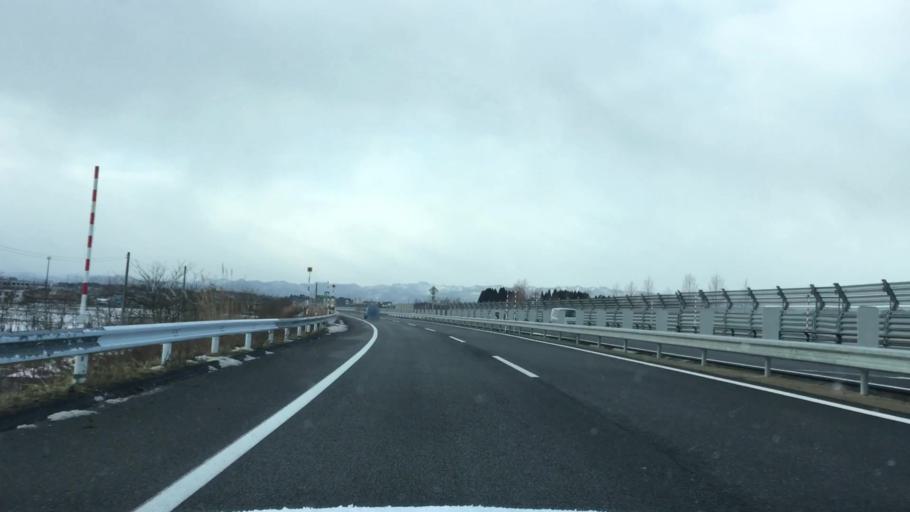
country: JP
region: Akita
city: Odate
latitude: 40.2992
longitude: 140.5556
